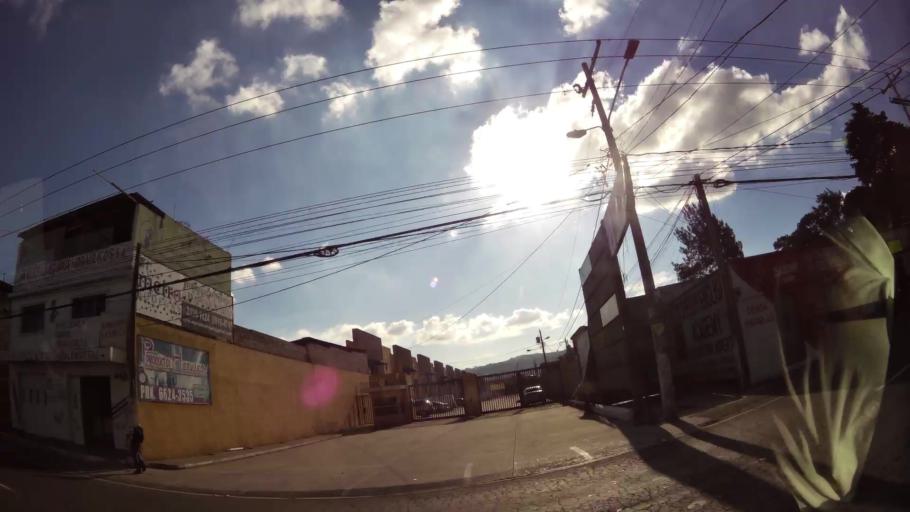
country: GT
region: Guatemala
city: Villa Nueva
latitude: 14.5170
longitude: -90.5786
